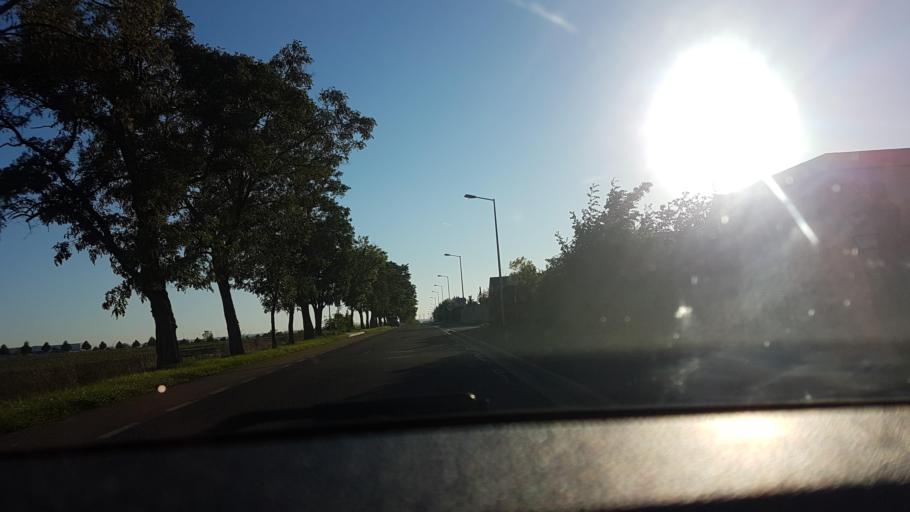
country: DE
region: Saxony-Anhalt
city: Bernburg
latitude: 51.7823
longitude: 11.7244
